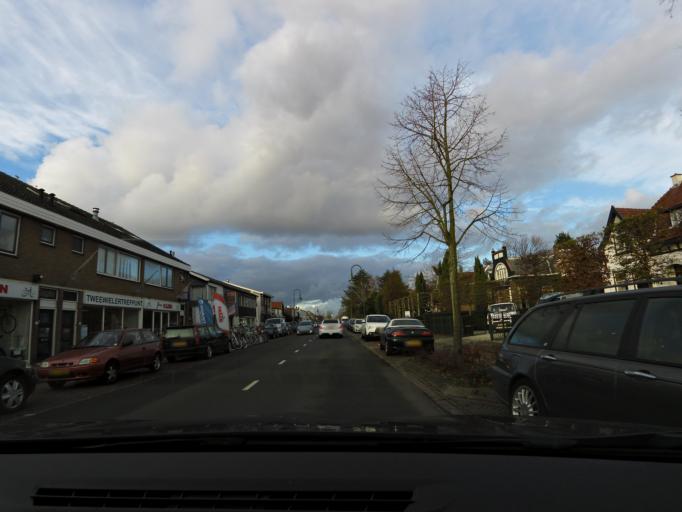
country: NL
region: North Brabant
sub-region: Gemeente Moerdijk
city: Willemstad
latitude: 51.7306
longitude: 4.4383
